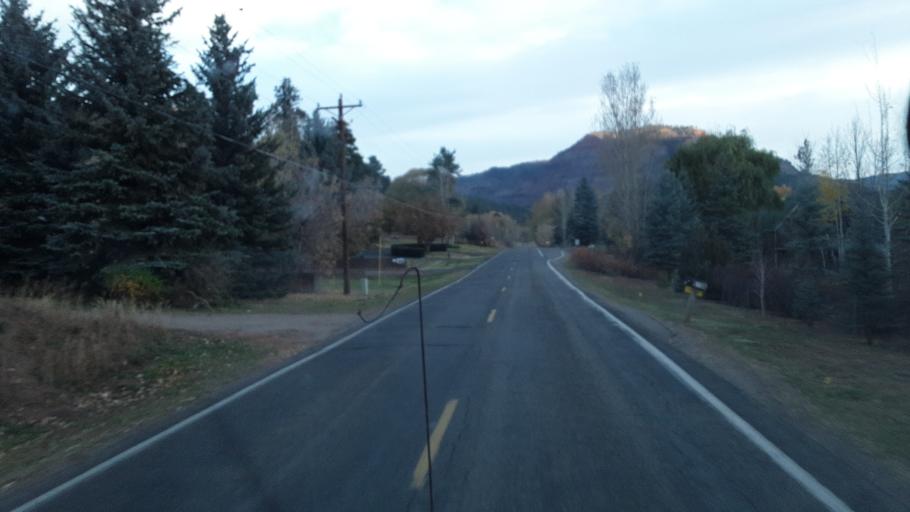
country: US
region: Colorado
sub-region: La Plata County
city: Durango
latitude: 37.3949
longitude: -107.8471
